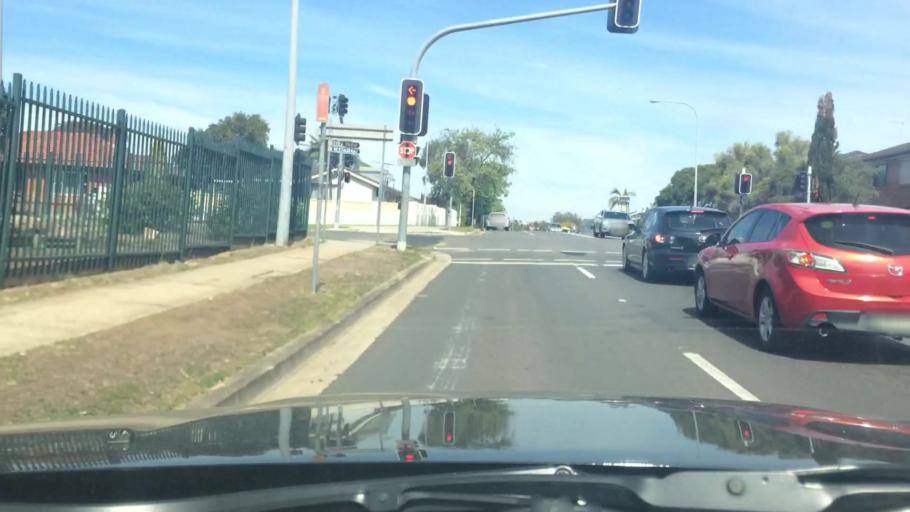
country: AU
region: New South Wales
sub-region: Fairfield
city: Cabramatta West
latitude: -33.8667
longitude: 150.8896
